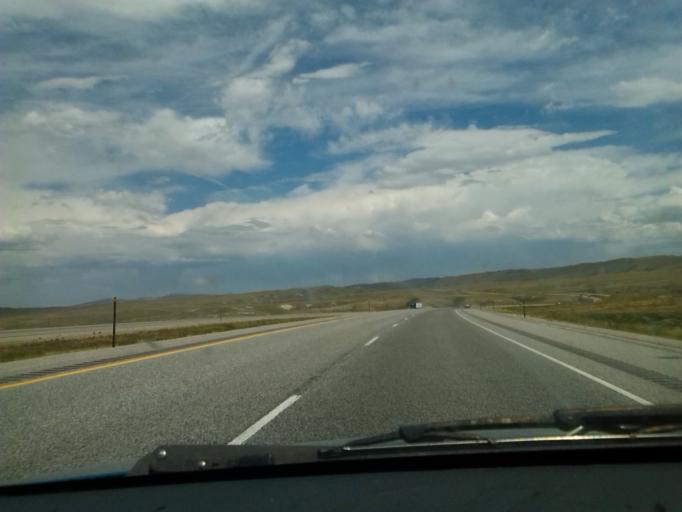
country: US
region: Wyoming
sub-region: Carbon County
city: Saratoga
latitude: 41.7394
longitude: -106.6220
